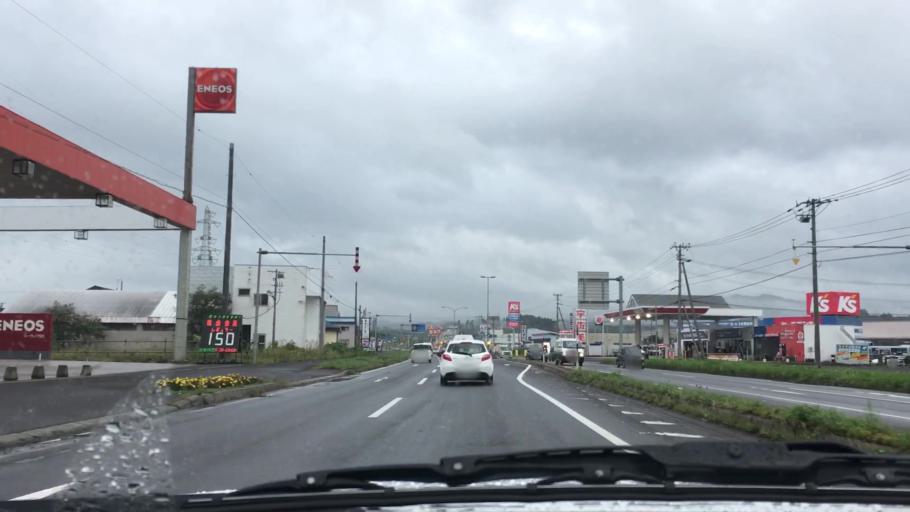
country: JP
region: Hokkaido
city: Nanae
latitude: 42.2513
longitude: 140.2851
